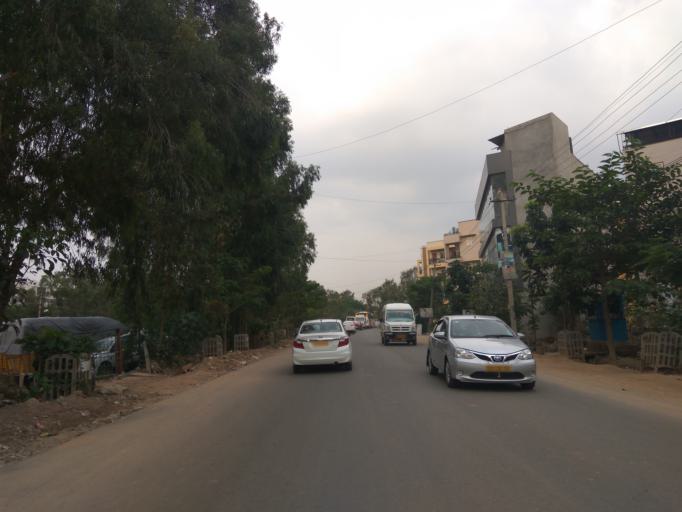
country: IN
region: Karnataka
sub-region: Bangalore Urban
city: Bangalore
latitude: 12.9730
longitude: 77.7018
